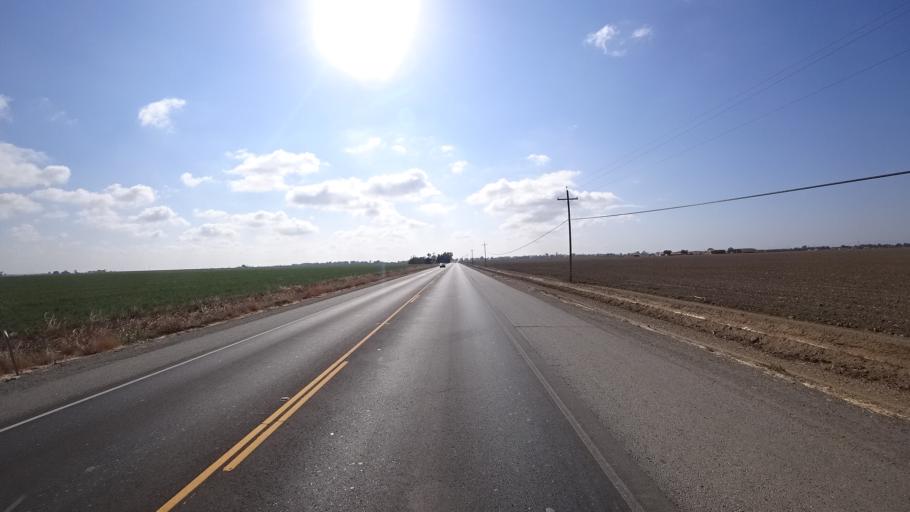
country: US
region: California
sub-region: Yolo County
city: Woodland
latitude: 38.7481
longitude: -121.7295
